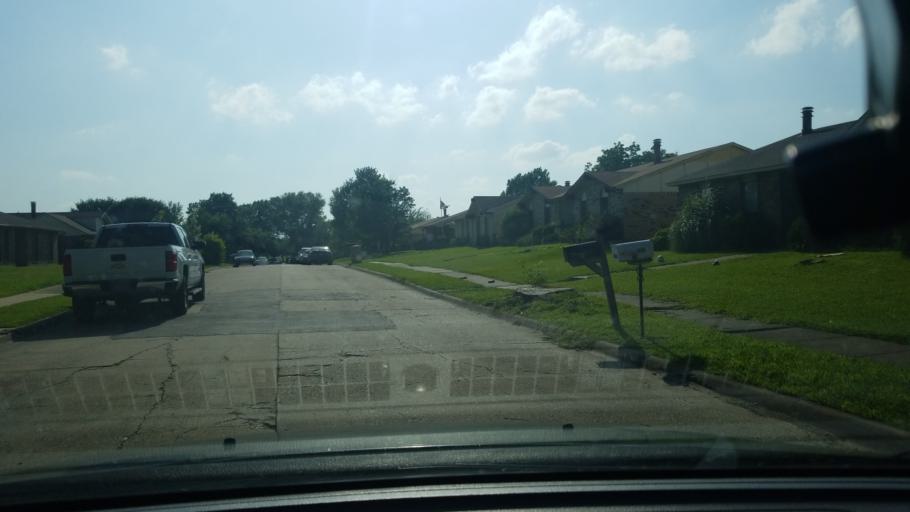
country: US
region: Texas
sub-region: Dallas County
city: Sunnyvale
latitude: 32.8184
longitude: -96.6034
